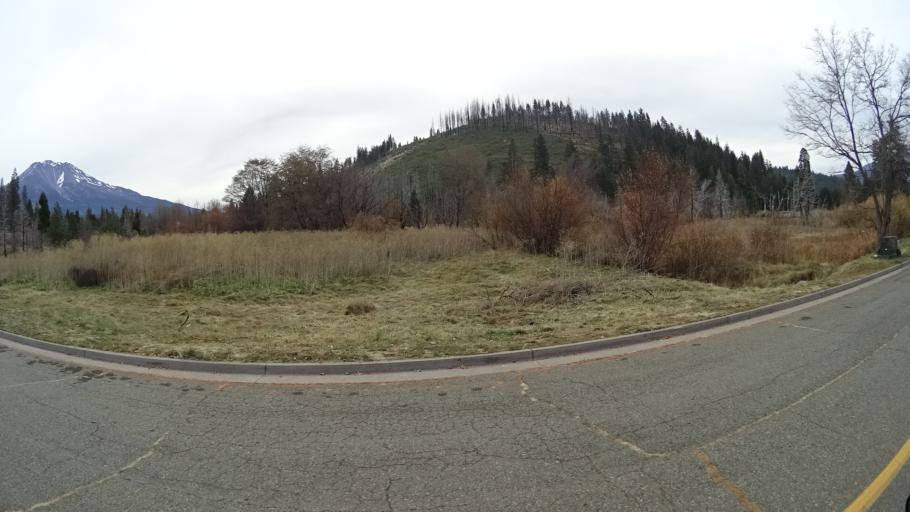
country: US
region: California
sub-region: Siskiyou County
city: Weed
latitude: 41.4216
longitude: -122.3803
